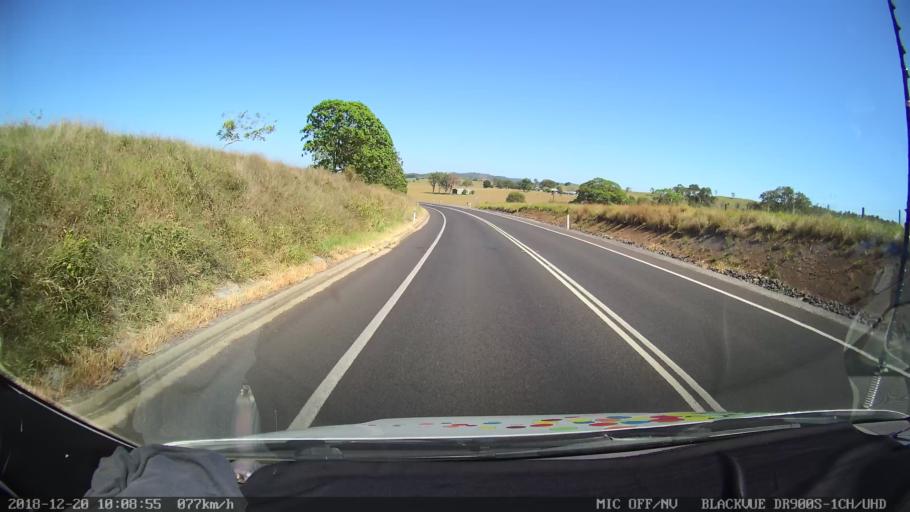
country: AU
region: New South Wales
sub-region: Lismore Municipality
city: Lismore
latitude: -28.8793
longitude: 153.1947
